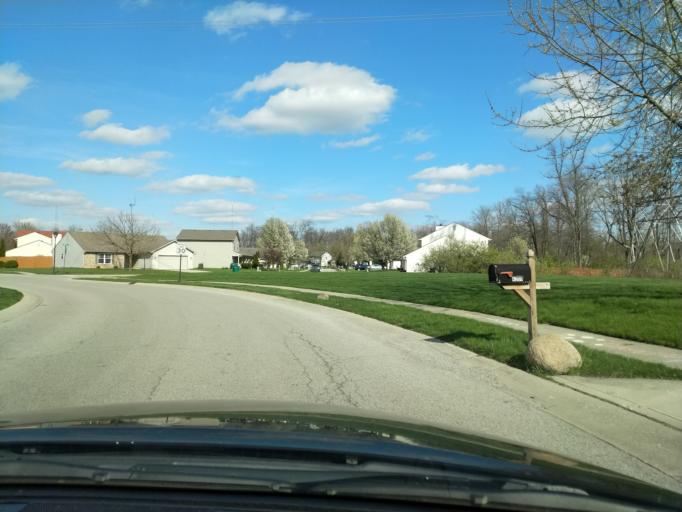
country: US
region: Indiana
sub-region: Boone County
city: Zionsville
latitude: 39.8864
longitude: -86.2319
